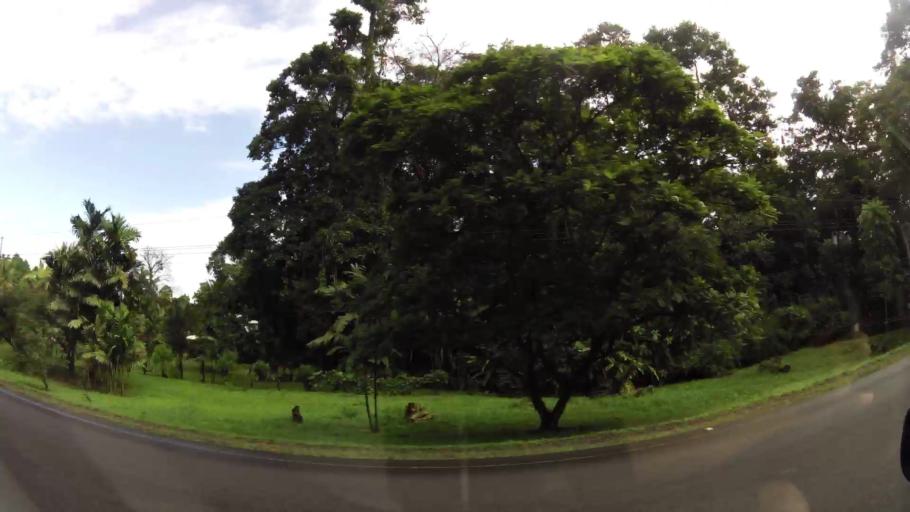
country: CR
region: Limon
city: Pocora
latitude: 10.1841
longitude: -83.6286
